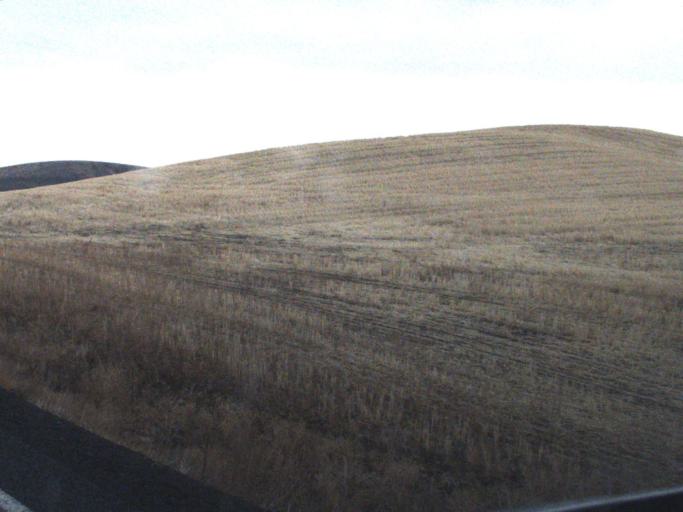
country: US
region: Washington
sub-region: Lincoln County
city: Davenport
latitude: 47.7224
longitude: -118.1522
